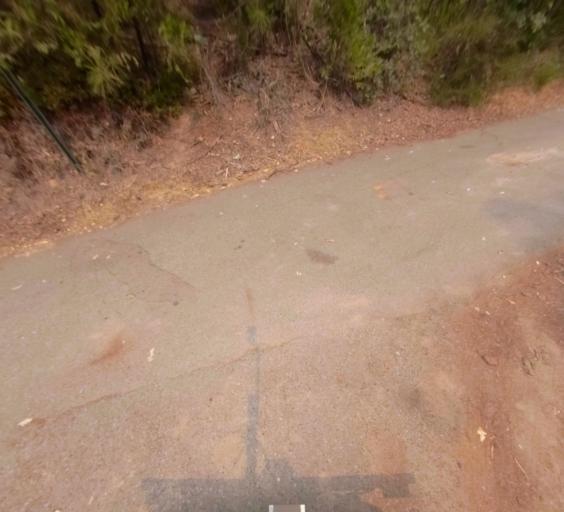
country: US
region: California
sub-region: Madera County
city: Oakhurst
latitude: 37.3184
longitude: -119.5544
